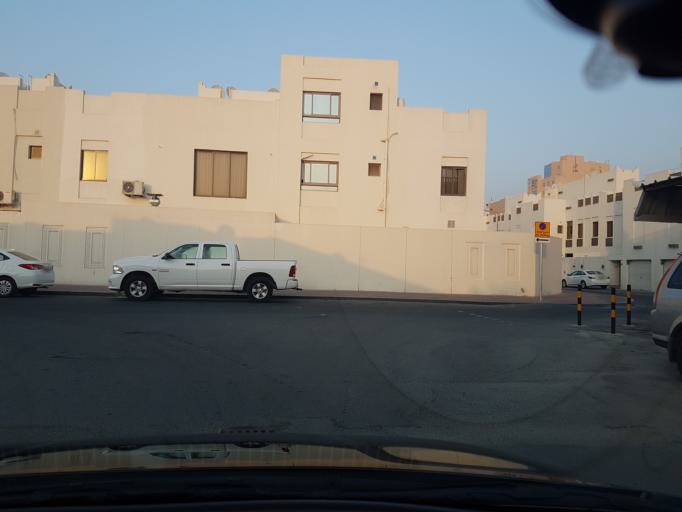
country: BH
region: Manama
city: Manama
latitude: 26.2015
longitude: 50.5934
